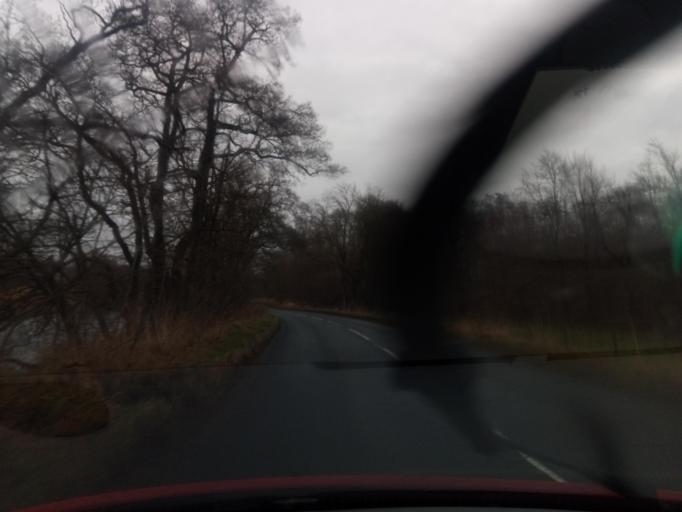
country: GB
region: England
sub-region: Northumberland
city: Rochester
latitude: 55.1651
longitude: -2.4113
